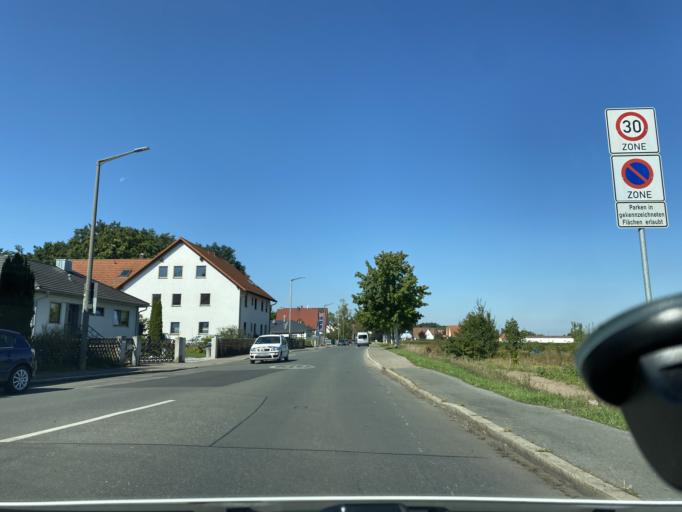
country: DE
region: Bavaria
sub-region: Regierungsbezirk Mittelfranken
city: Furth
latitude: 49.4979
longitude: 11.0036
